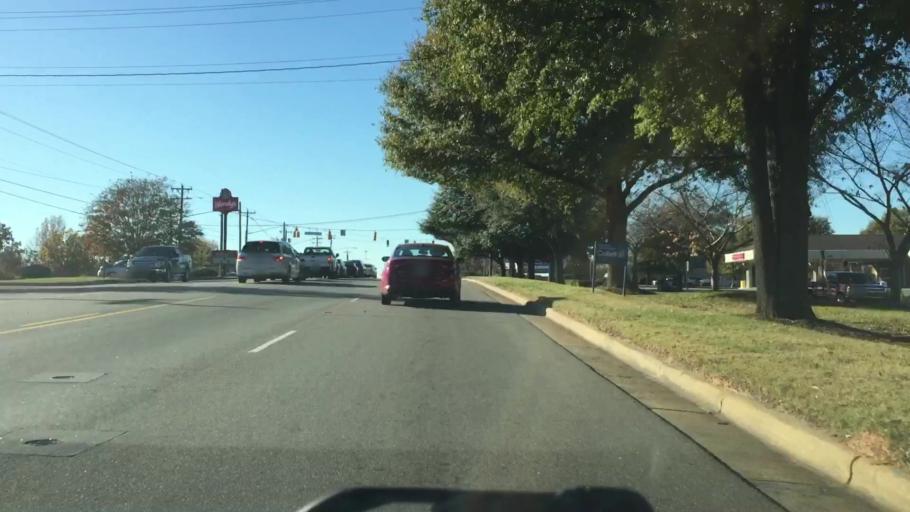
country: US
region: North Carolina
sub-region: Iredell County
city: Mooresville
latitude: 35.5934
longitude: -80.8550
